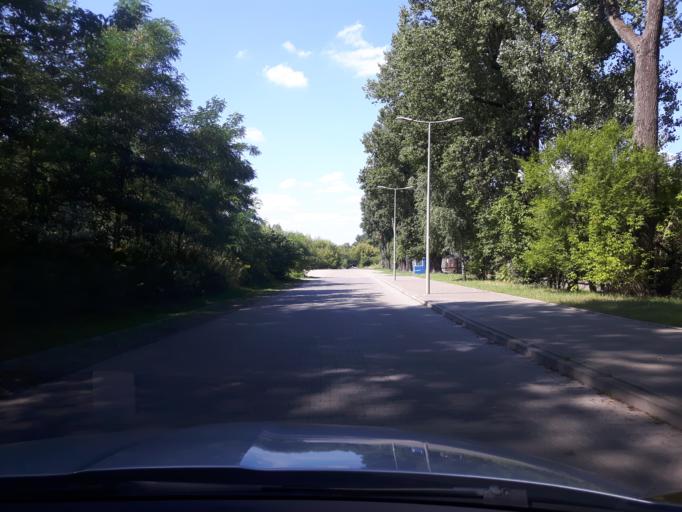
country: PL
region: Masovian Voivodeship
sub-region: Powiat wolominski
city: Zabki
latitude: 52.2697
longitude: 21.0953
